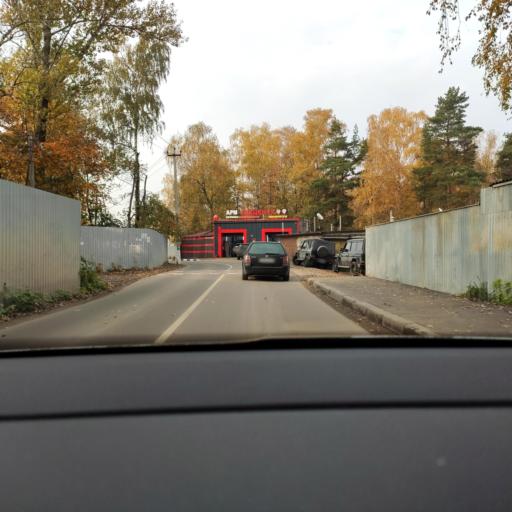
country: RU
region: Moskovskaya
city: Ivanteyevka
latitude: 55.9651
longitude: 37.9494
